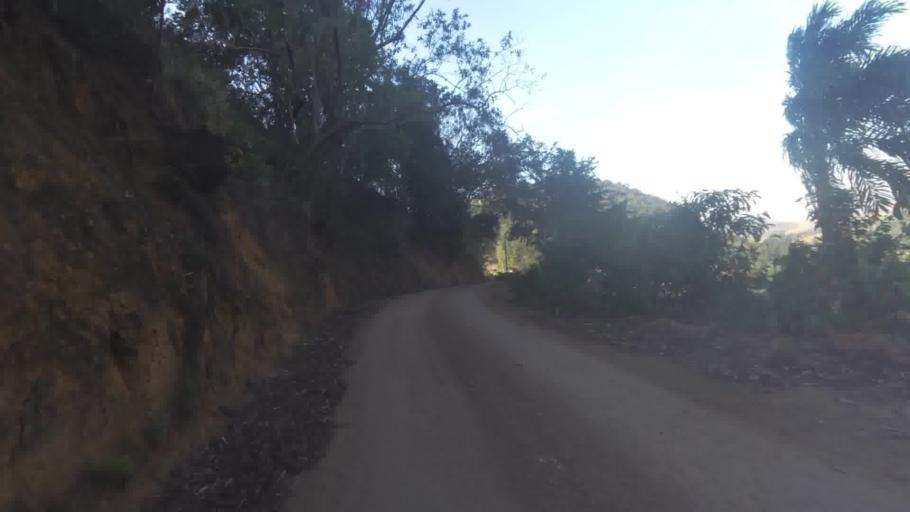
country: BR
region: Espirito Santo
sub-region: Iconha
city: Iconha
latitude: -20.7482
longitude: -40.7991
